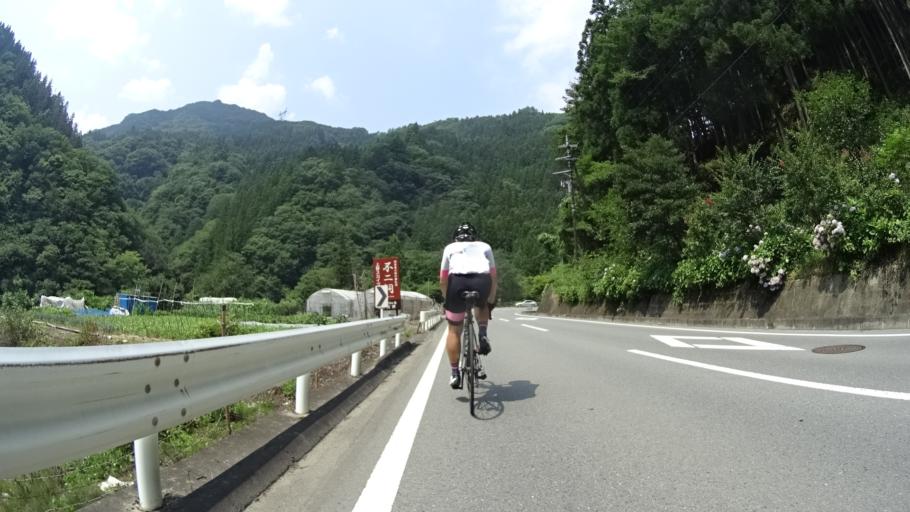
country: JP
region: Gunma
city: Tomioka
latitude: 36.0768
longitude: 138.7808
